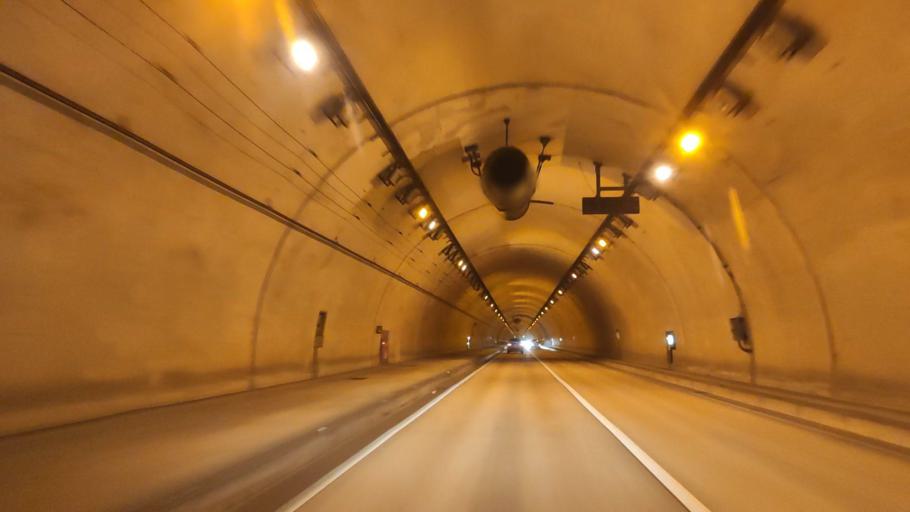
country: JP
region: Ehime
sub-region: Shikoku-chuo Shi
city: Matsuyama
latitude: 33.8769
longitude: 132.7138
